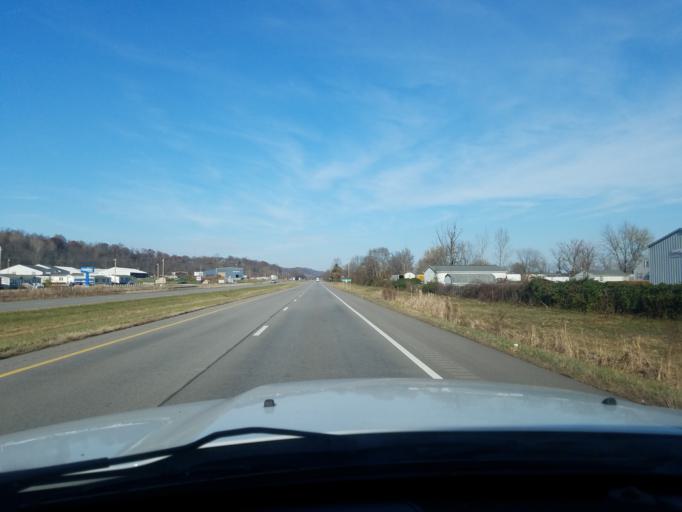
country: US
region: West Virginia
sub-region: Wood County
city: Vienna
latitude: 39.3162
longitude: -81.5642
